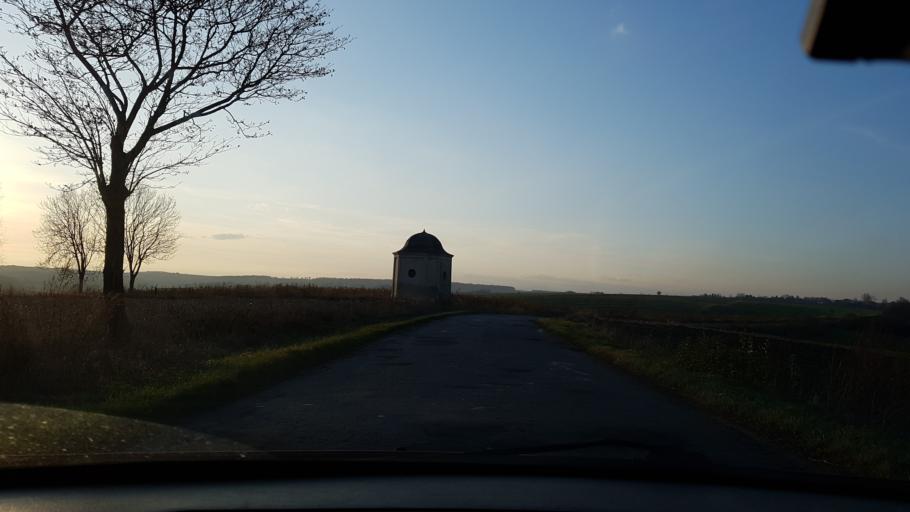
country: PL
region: Lower Silesian Voivodeship
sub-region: Powiat zabkowicki
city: Henrykow
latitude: 50.6592
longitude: 16.9989
